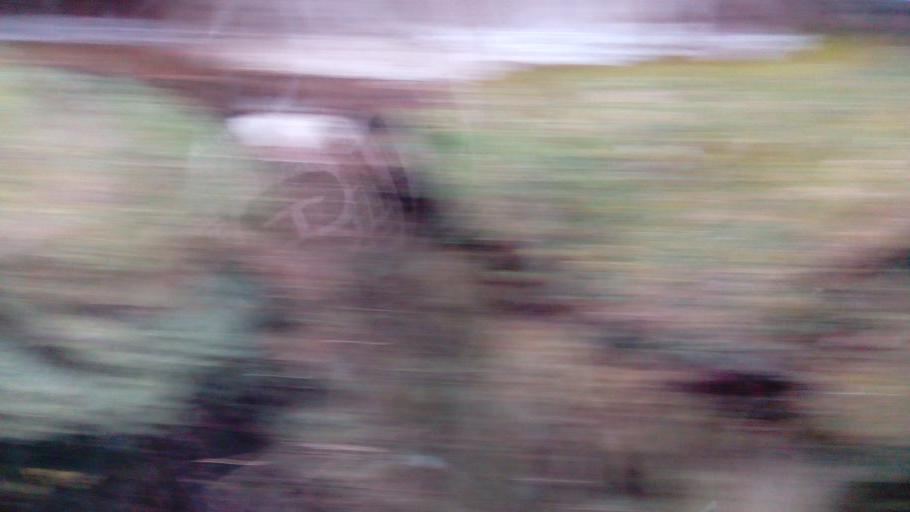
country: TW
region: Taiwan
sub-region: Hualien
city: Hualian
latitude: 24.3922
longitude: 121.3535
